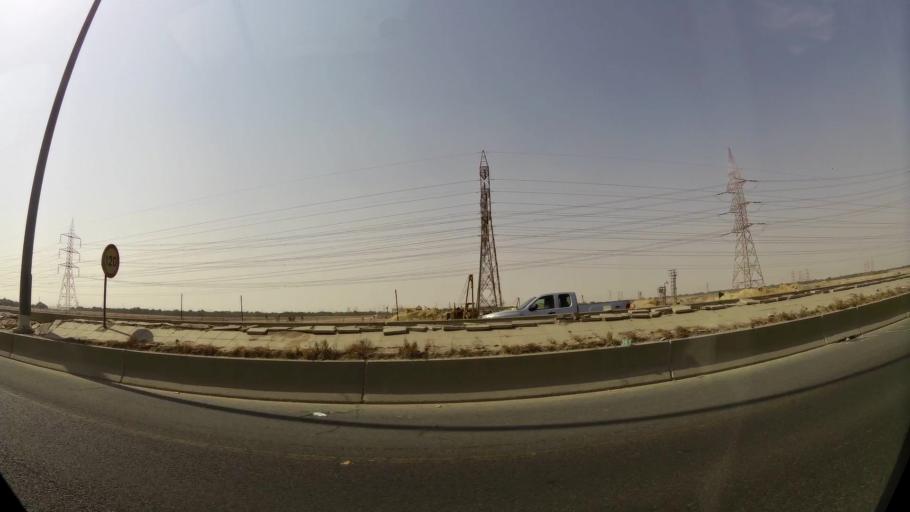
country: KW
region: Al Ahmadi
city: Al Fahahil
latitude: 29.0544
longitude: 48.1104
